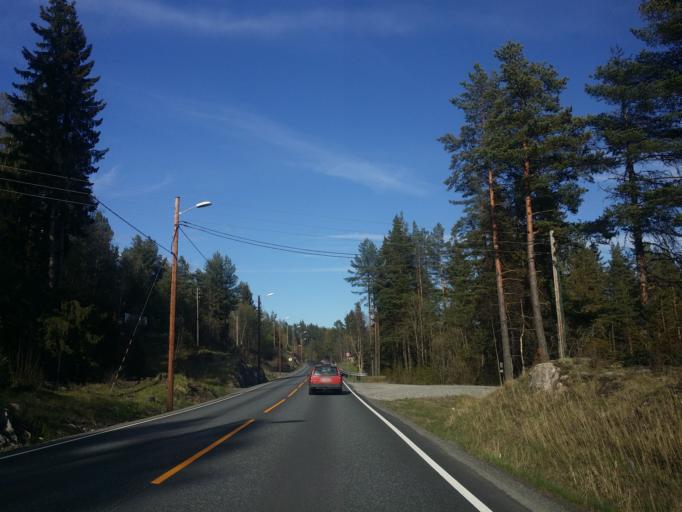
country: NO
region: Buskerud
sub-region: Kongsberg
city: Kongsberg
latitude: 59.6288
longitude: 9.4900
